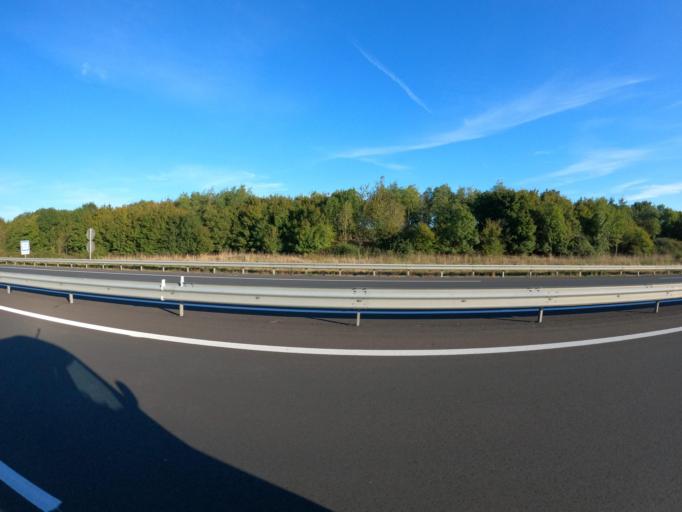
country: FR
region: Pays de la Loire
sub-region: Departement de la Vendee
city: La Gaubretiere
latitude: 46.9075
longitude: -1.0492
